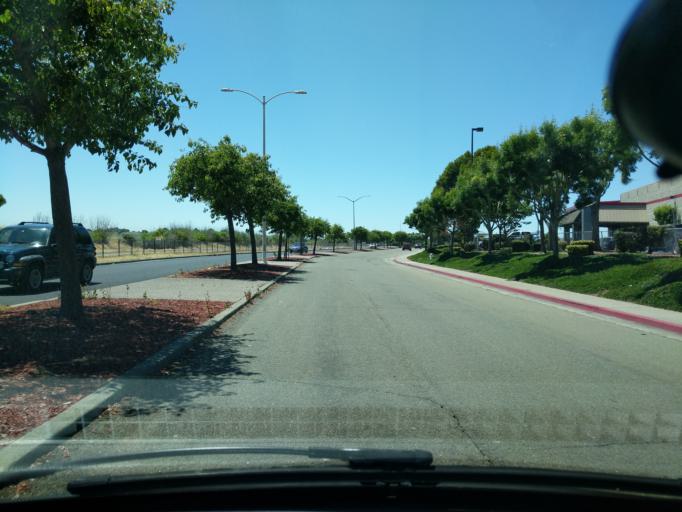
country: US
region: California
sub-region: Contra Costa County
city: El Cerrito
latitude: 37.8984
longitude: -122.3193
